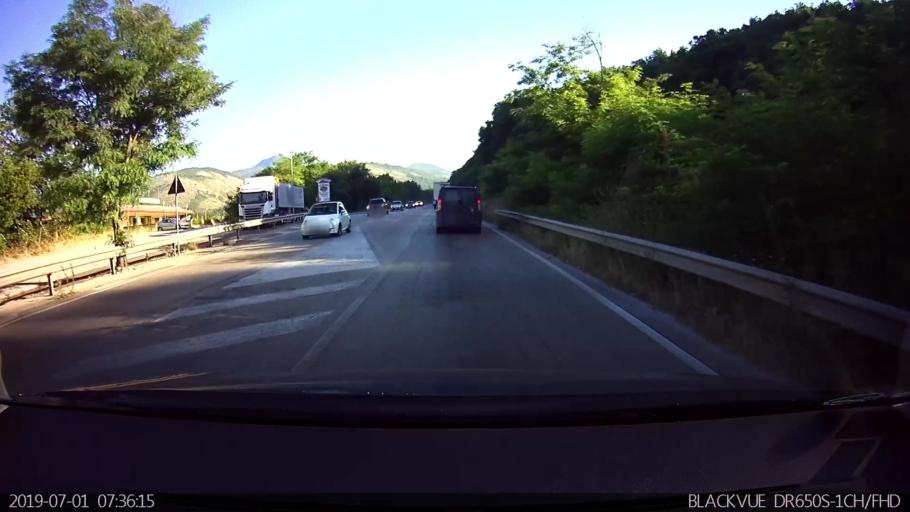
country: IT
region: Latium
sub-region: Provincia di Latina
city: Prossedi
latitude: 41.5302
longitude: 13.2675
